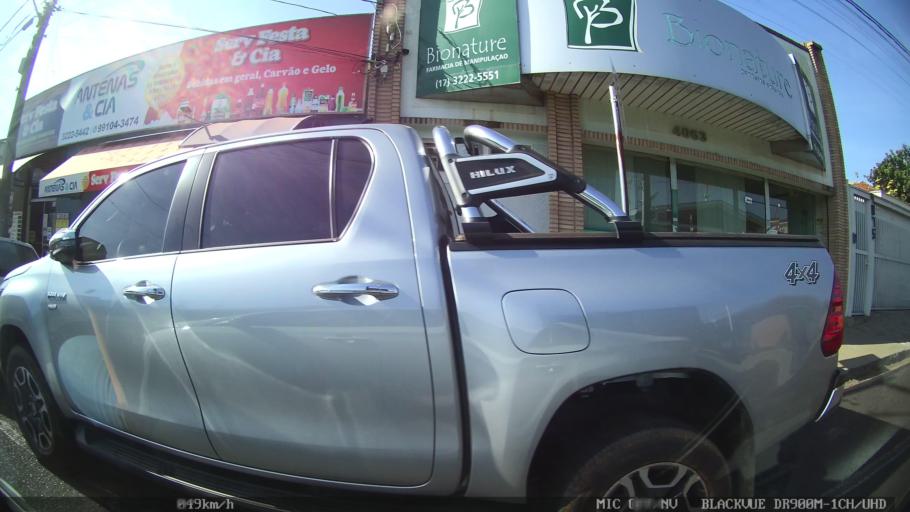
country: BR
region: Sao Paulo
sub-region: Sao Jose Do Rio Preto
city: Sao Jose do Rio Preto
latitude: -20.8217
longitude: -49.3765
